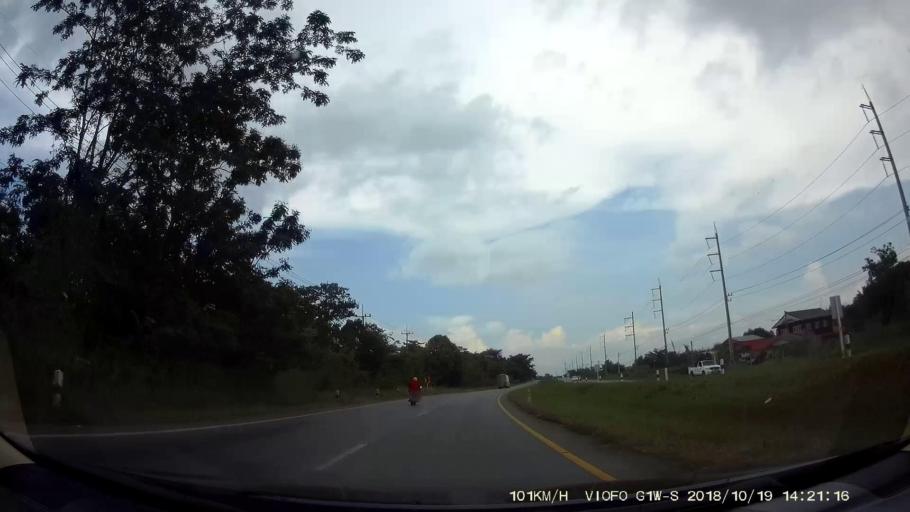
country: TH
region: Chaiyaphum
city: Kaeng Khro
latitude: 16.0505
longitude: 102.2644
